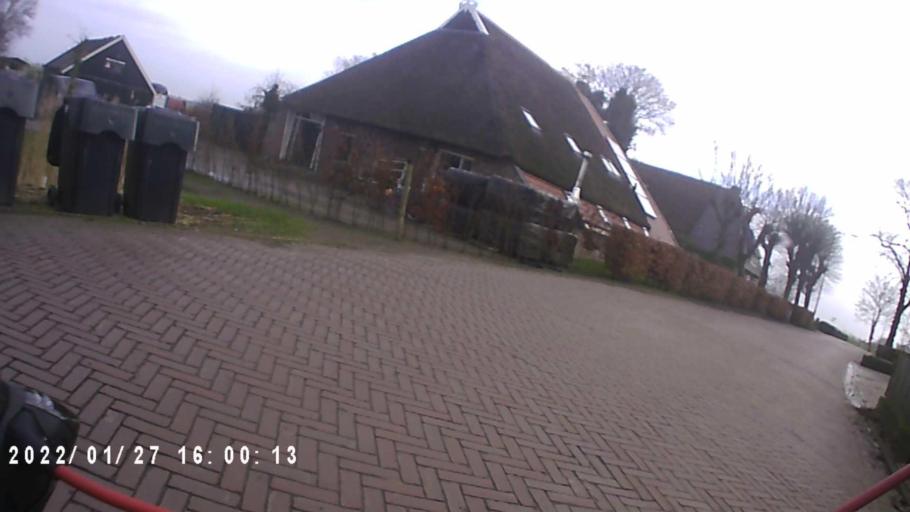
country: NL
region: Friesland
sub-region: Gemeente Dongeradeel
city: Anjum
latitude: 53.3729
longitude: 6.0899
